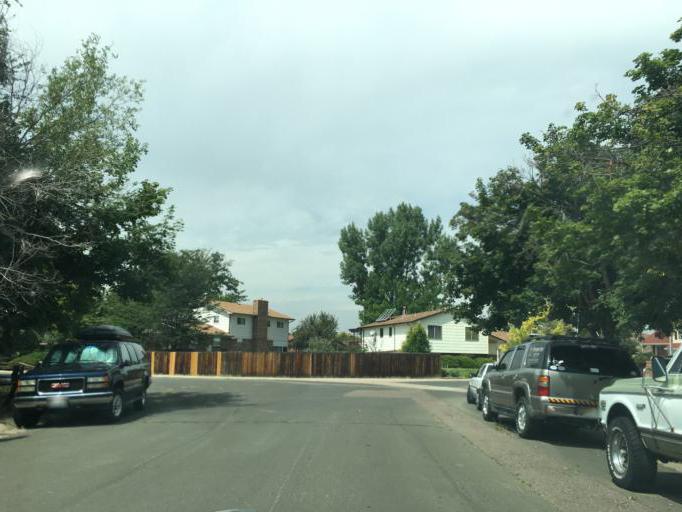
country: US
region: Colorado
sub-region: Adams County
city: Aurora
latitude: 39.7295
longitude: -104.8031
